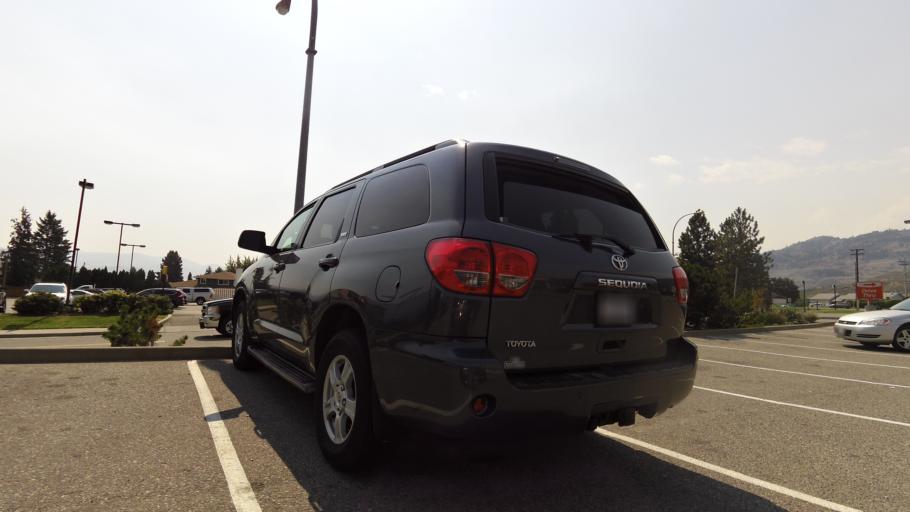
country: CA
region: British Columbia
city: Osoyoos
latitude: 49.0341
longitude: -119.4741
